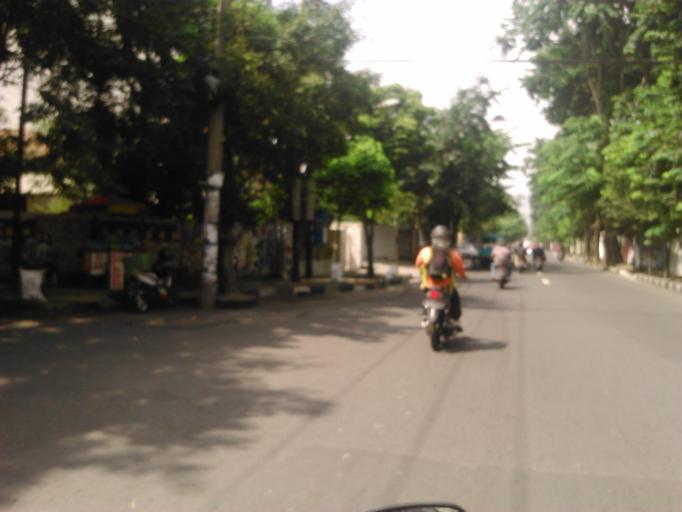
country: ID
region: East Java
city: Gubengairlangga
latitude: -7.2736
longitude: 112.7499
